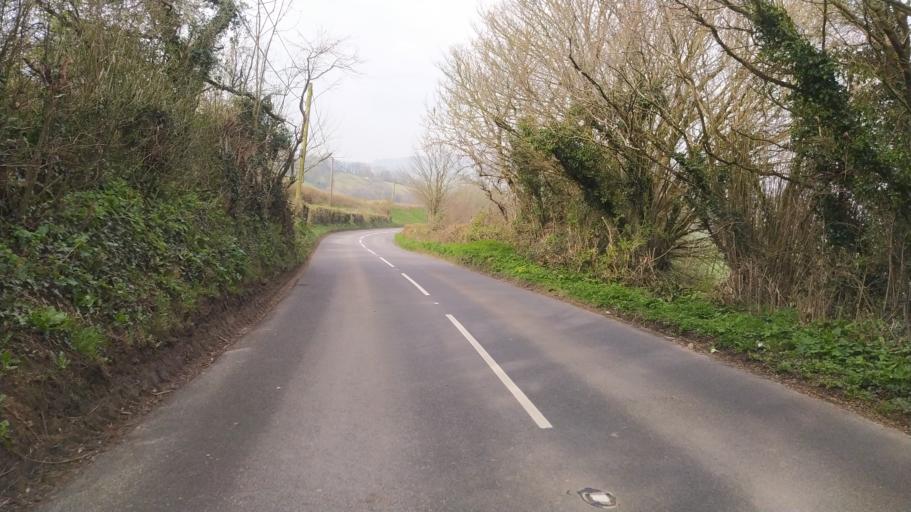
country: GB
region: England
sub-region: Dorset
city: Beaminster
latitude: 50.8022
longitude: -2.7185
